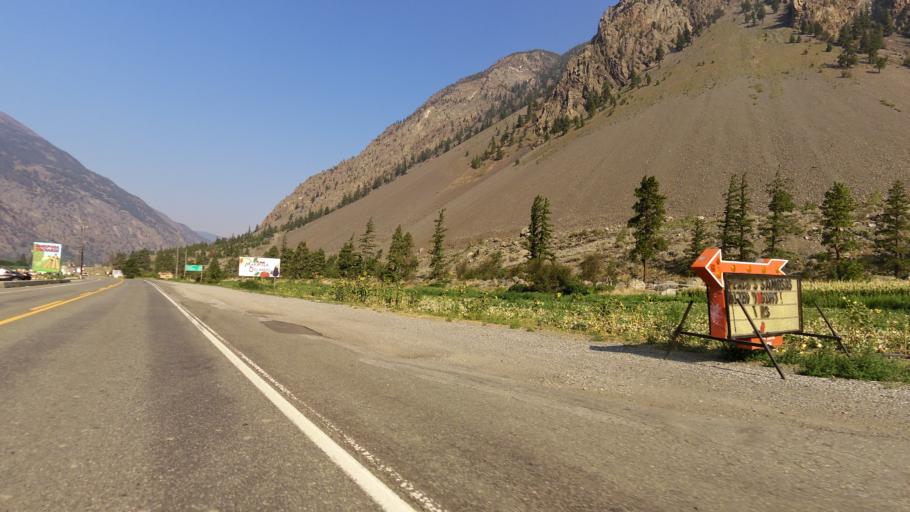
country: CA
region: British Columbia
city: Oliver
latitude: 49.2053
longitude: -119.8543
